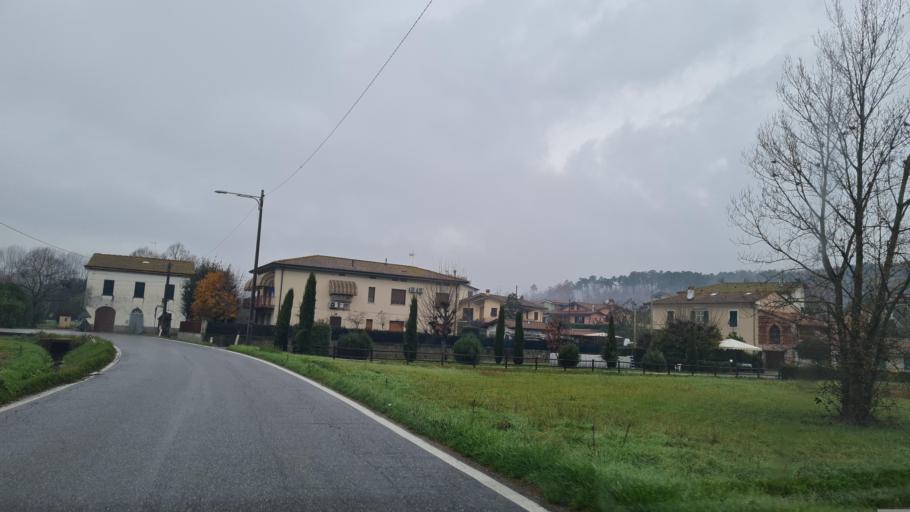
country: IT
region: Tuscany
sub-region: Provincia di Lucca
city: Lucca
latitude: 43.8588
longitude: 10.4522
